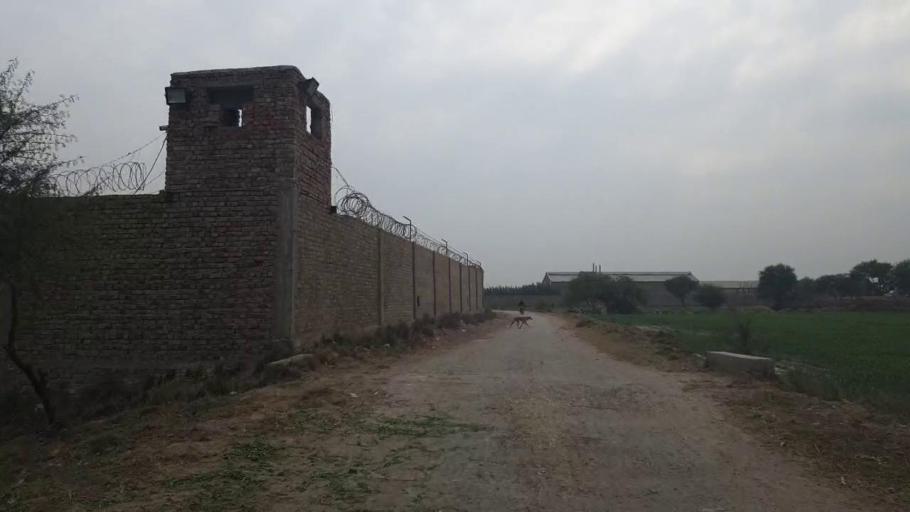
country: PK
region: Sindh
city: Shahdadpur
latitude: 25.9373
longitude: 68.7012
